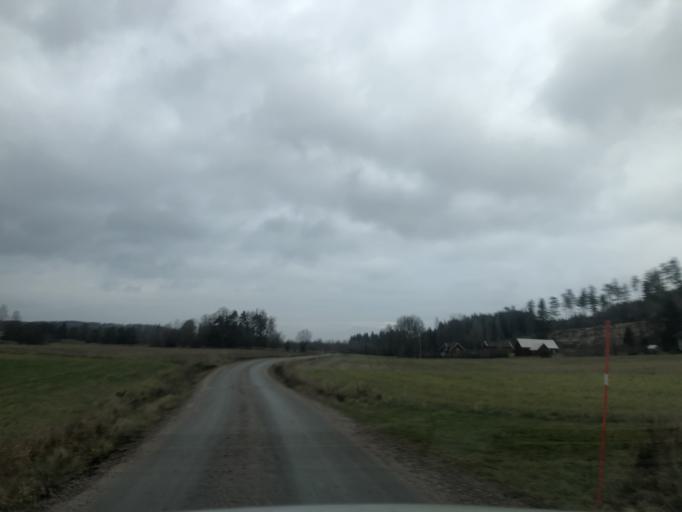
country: SE
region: Vaestra Goetaland
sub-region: Ulricehamns Kommun
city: Ulricehamn
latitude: 57.8889
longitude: 13.4677
